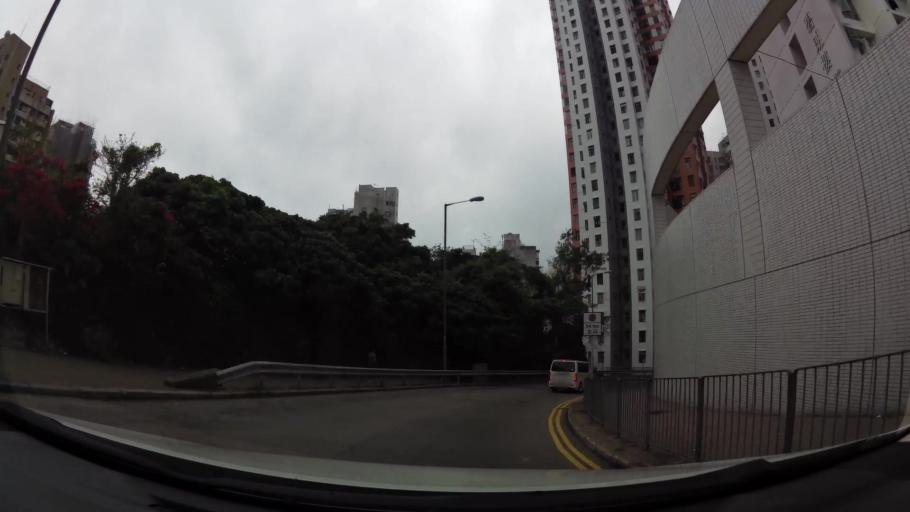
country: HK
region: Central and Western
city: Central
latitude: 22.2480
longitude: 114.1572
